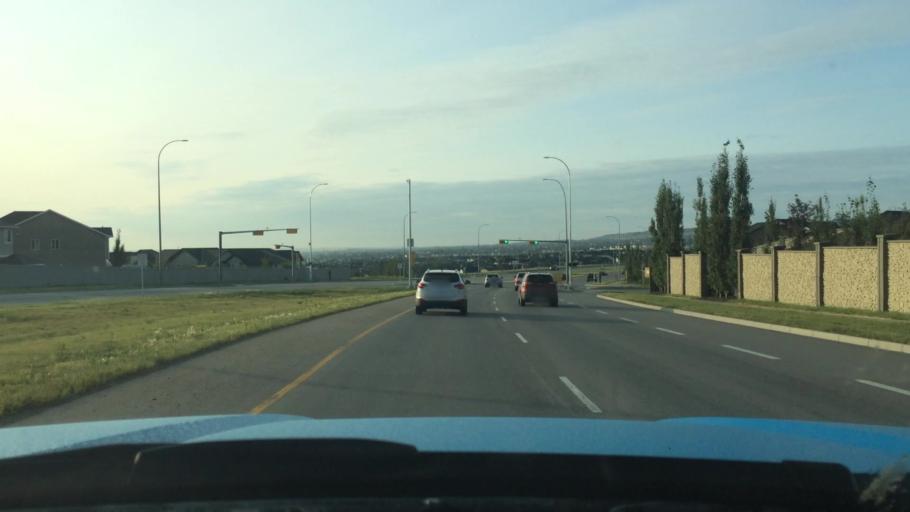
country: CA
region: Alberta
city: Calgary
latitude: 51.1640
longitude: -114.1450
